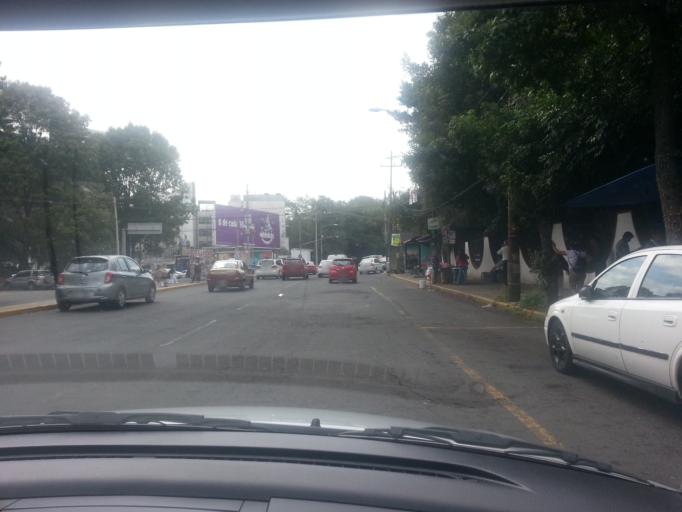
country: MX
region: Mexico City
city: Coyoacan
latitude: 19.3517
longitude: -99.1768
